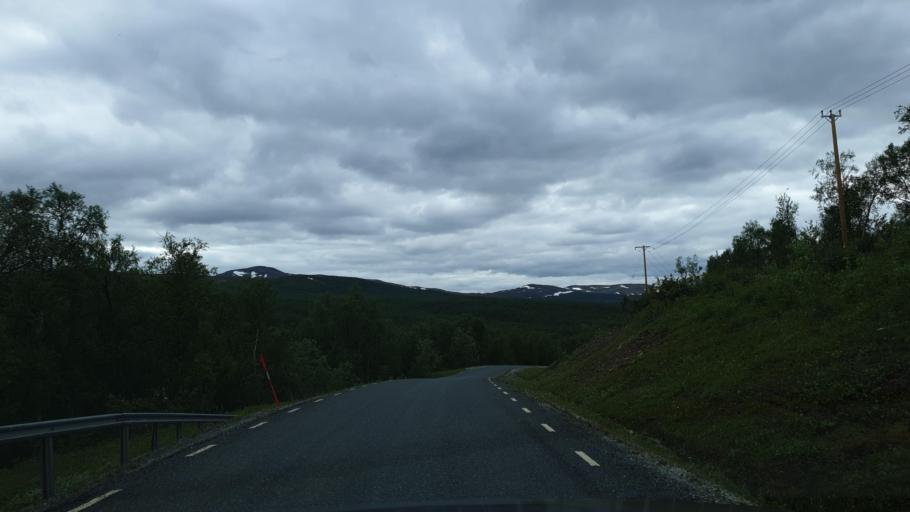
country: NO
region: Nordland
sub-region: Hattfjelldal
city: Hattfjelldal
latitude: 65.4190
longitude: 14.7980
